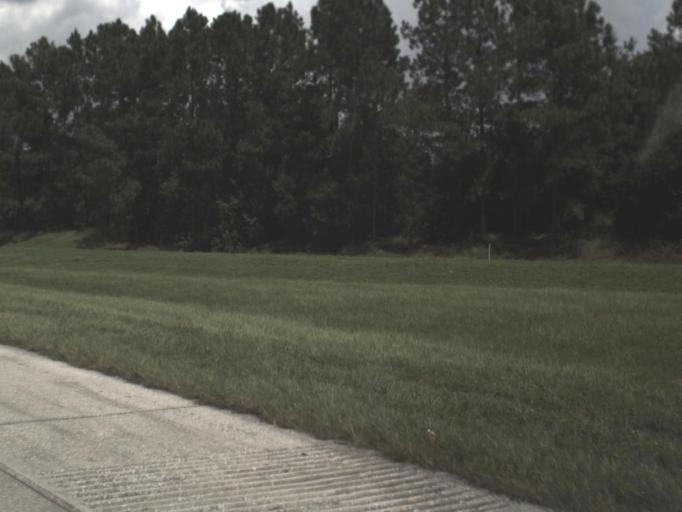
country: US
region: Florida
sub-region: Hillsborough County
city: Mango
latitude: 27.9854
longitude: -82.3261
